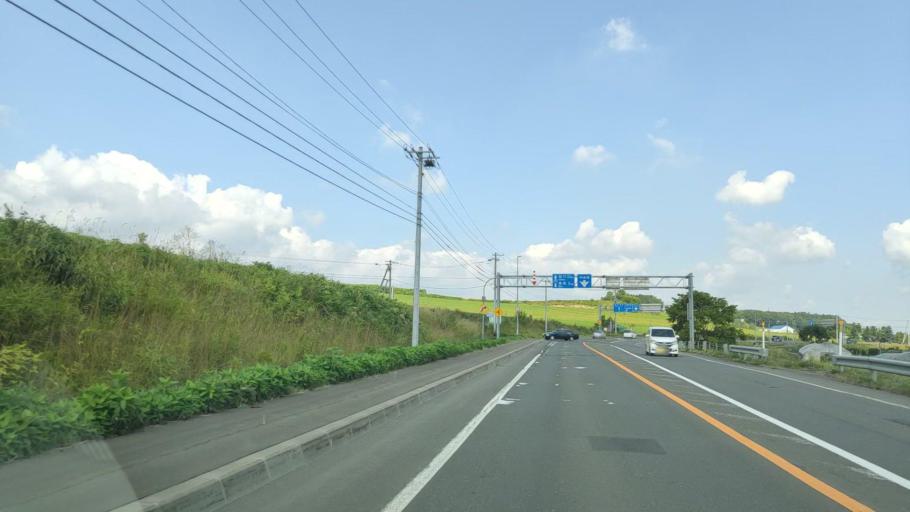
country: JP
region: Hokkaido
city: Shimo-furano
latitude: 43.5321
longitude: 142.4420
